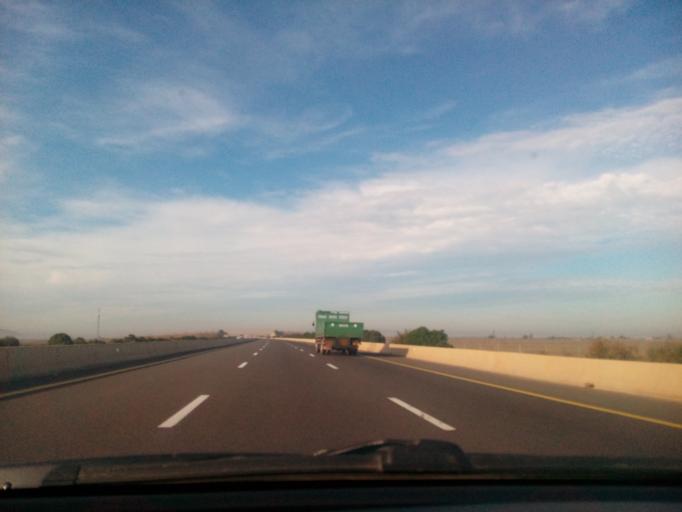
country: DZ
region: Mascara
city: Sig
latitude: 35.5876
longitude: -0.1098
